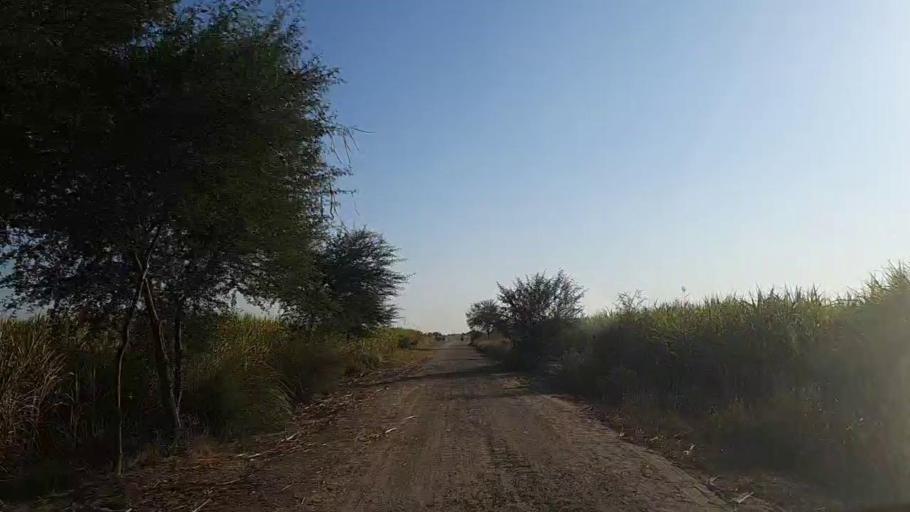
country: PK
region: Sindh
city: Khadro
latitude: 26.2689
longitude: 68.8603
